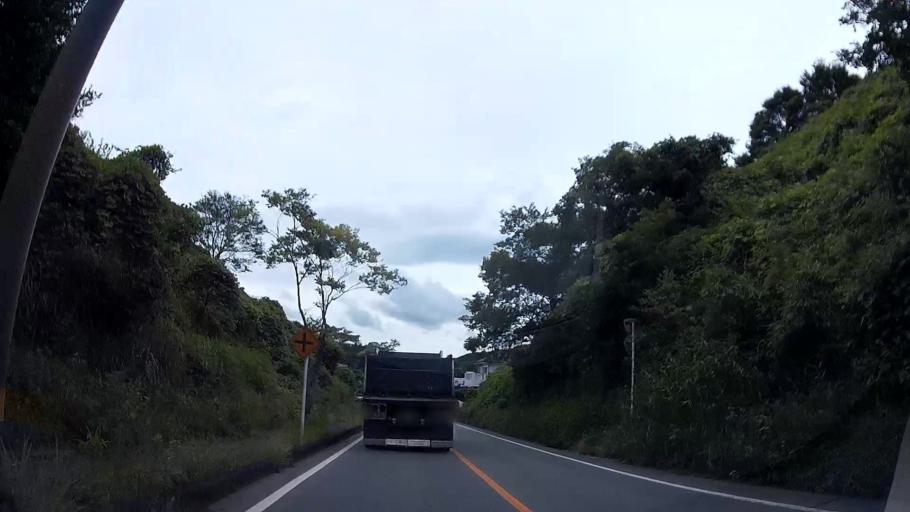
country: JP
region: Oita
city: Tsukawaki
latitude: 33.1256
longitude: 131.0612
